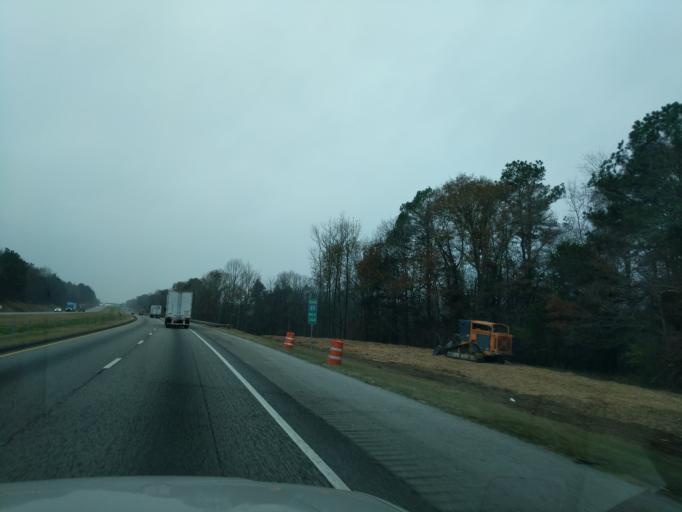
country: US
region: Georgia
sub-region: Banks County
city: Maysville
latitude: 34.2109
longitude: -83.5392
